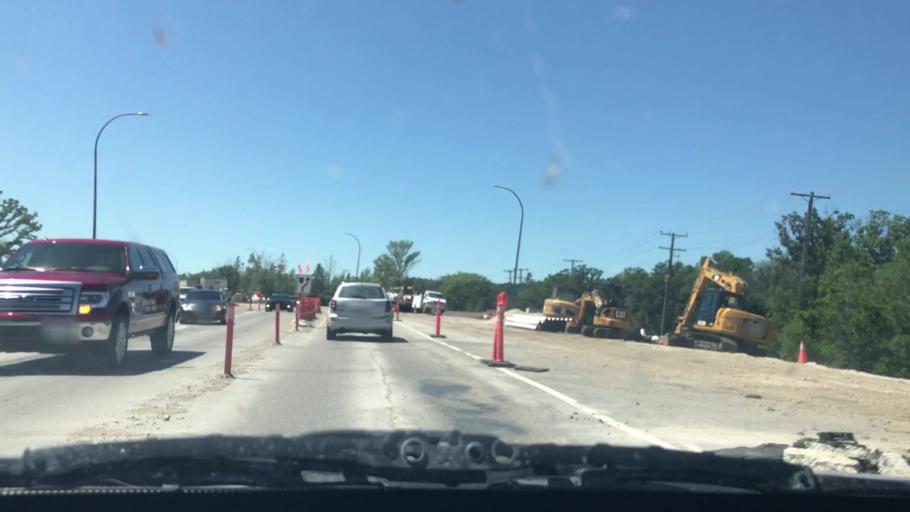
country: CA
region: Manitoba
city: Winnipeg
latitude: 49.8579
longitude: -97.0963
